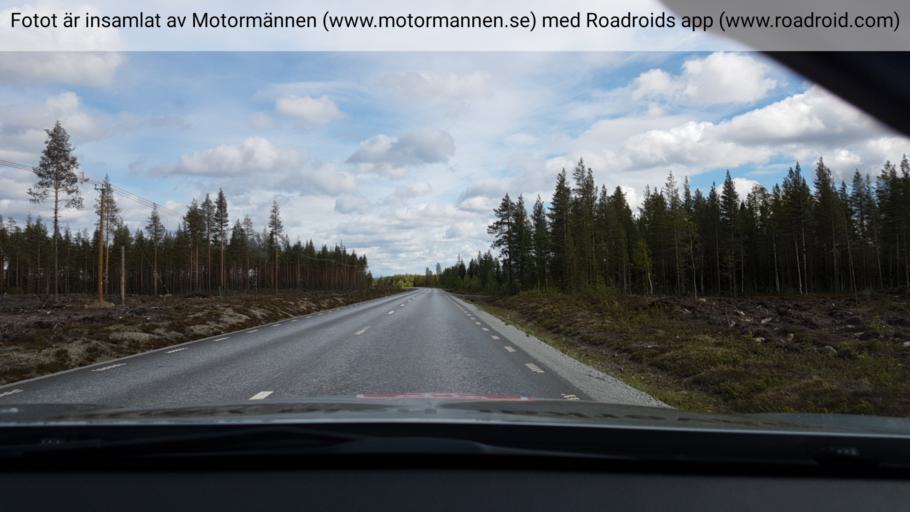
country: SE
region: Vaesterbotten
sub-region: Asele Kommun
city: Insjon
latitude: 64.1215
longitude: 18.0925
